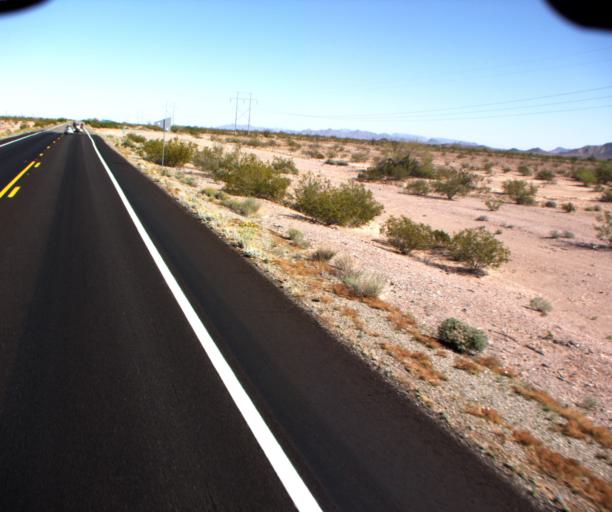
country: US
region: Arizona
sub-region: La Paz County
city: Quartzsite
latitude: 33.3102
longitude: -114.2169
